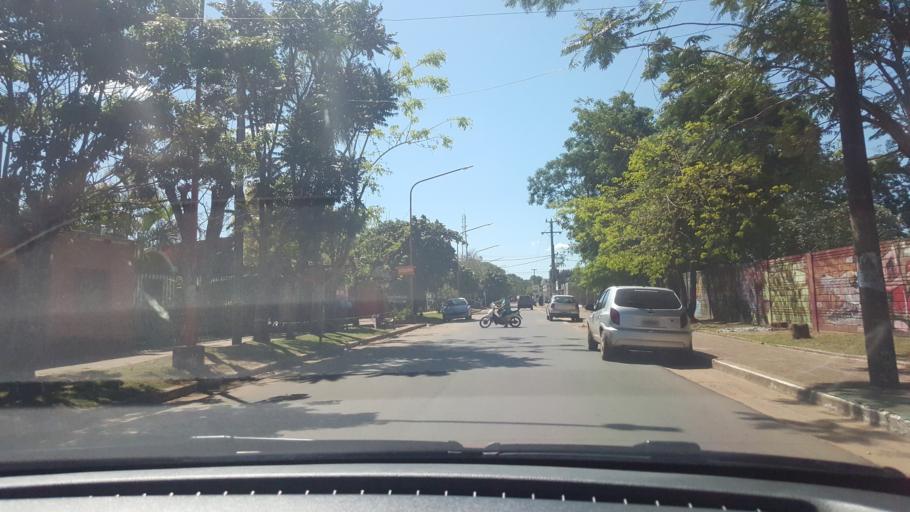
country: AR
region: Corrientes
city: Ituzaingo
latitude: -27.5911
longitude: -56.6870
